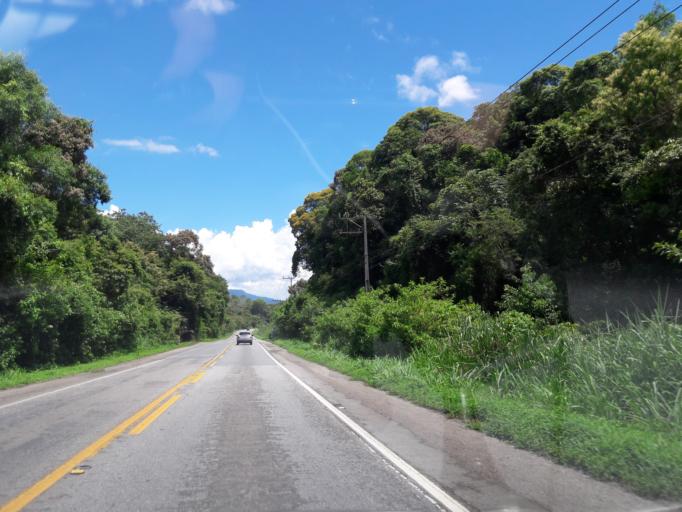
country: BR
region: Parana
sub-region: Antonina
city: Antonina
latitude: -25.4448
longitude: -48.7975
